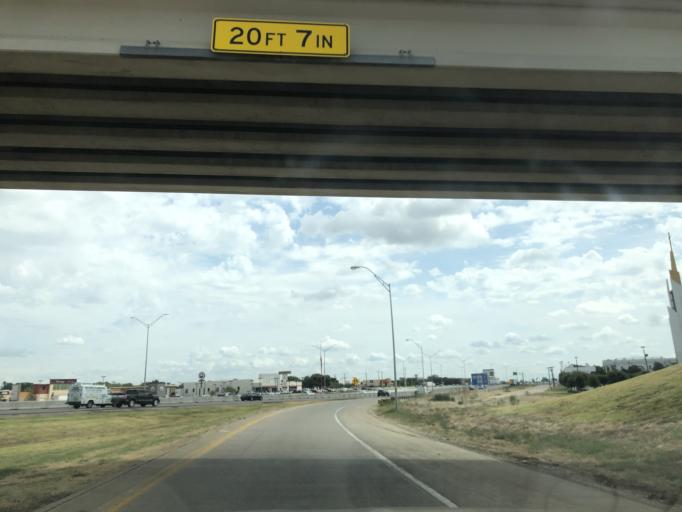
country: US
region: Texas
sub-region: Dallas County
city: Irving
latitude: 32.8364
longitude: -96.9897
